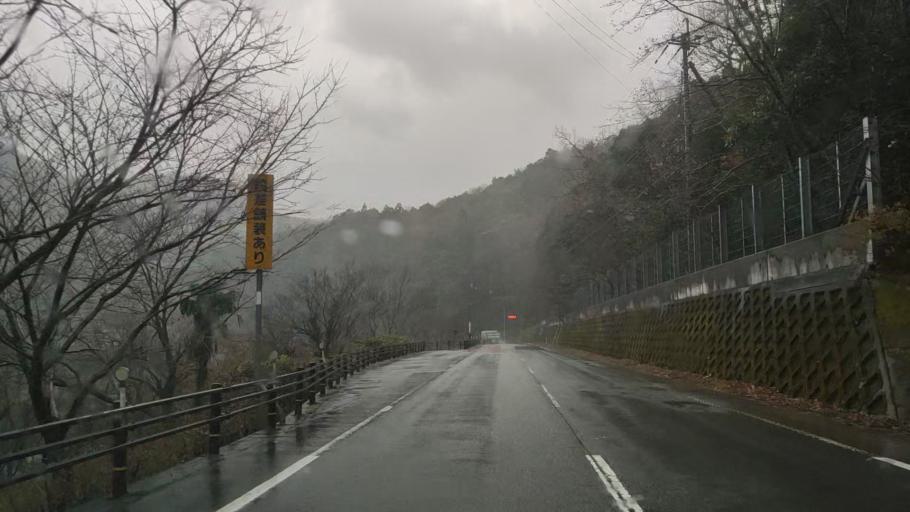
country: JP
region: Tokushima
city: Kamojimacho-jogejima
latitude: 34.1494
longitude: 134.3529
